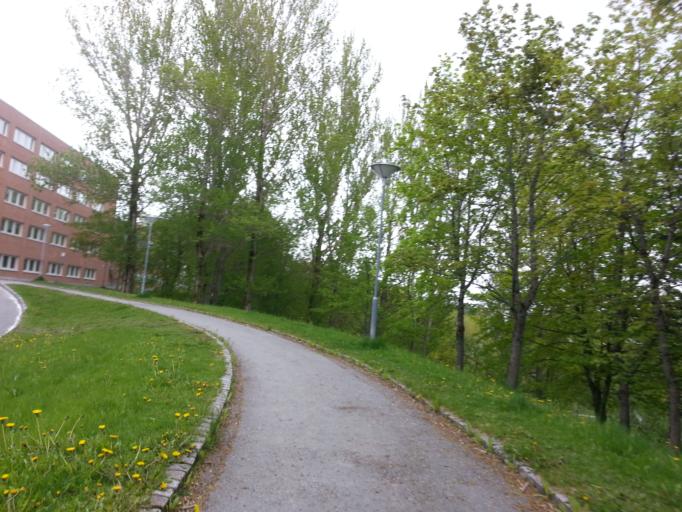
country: NO
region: Sor-Trondelag
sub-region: Trondheim
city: Trondheim
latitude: 63.4173
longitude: 10.4014
